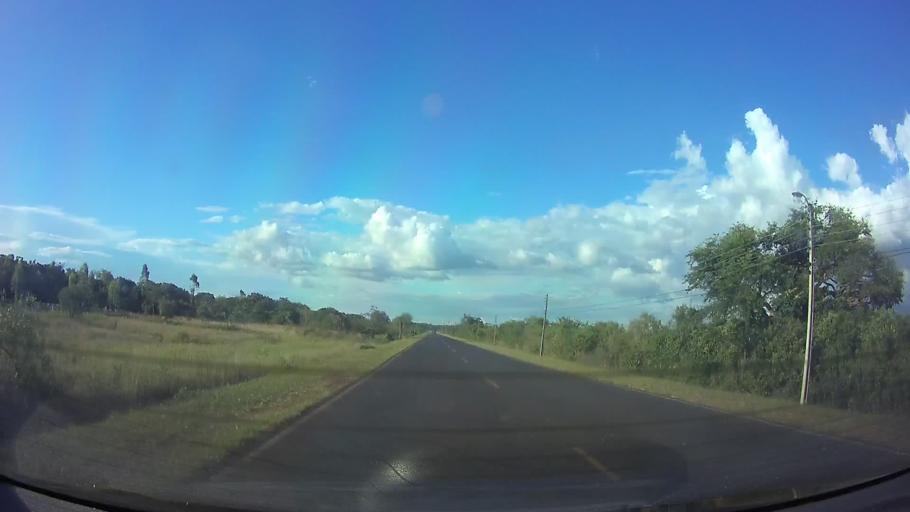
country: PY
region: Cordillera
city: Emboscada
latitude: -25.1521
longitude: -57.2610
